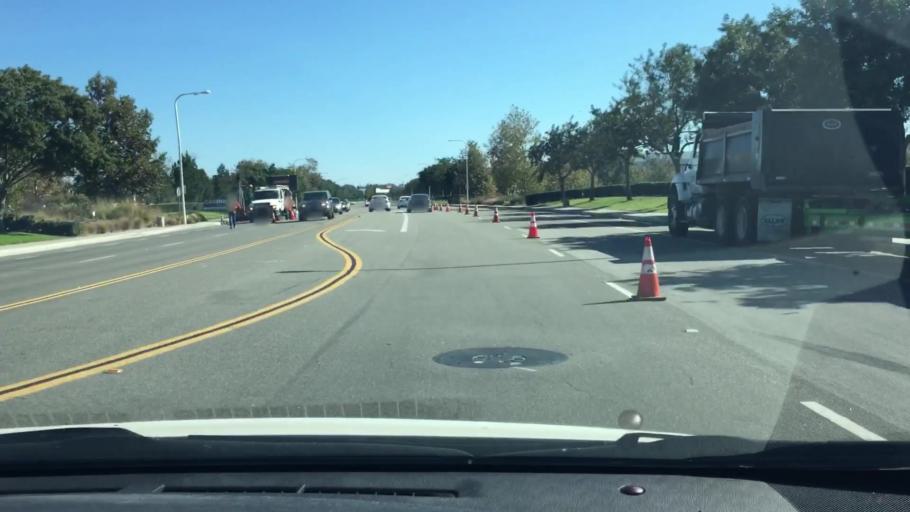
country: US
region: California
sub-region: Orange County
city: Laguna Woods
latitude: 33.6362
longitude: -117.7343
